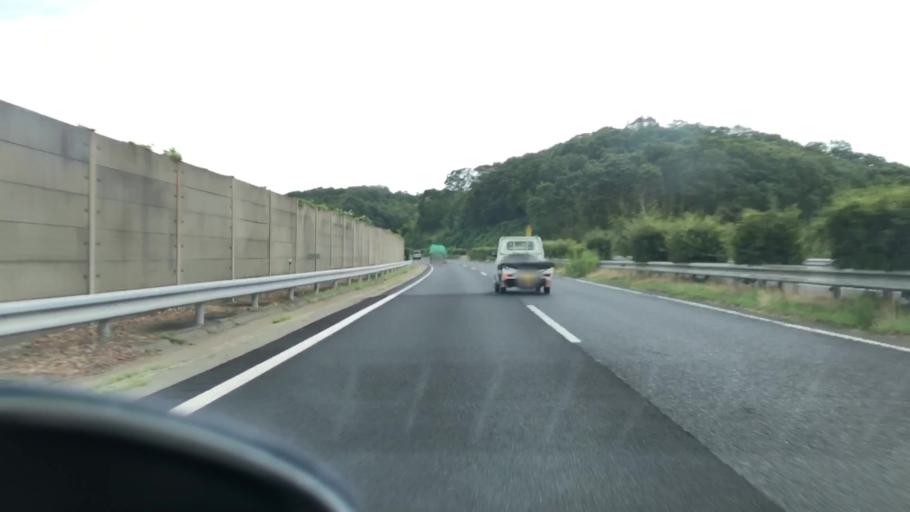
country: JP
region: Hyogo
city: Yashiro
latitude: 34.9119
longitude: 135.0412
